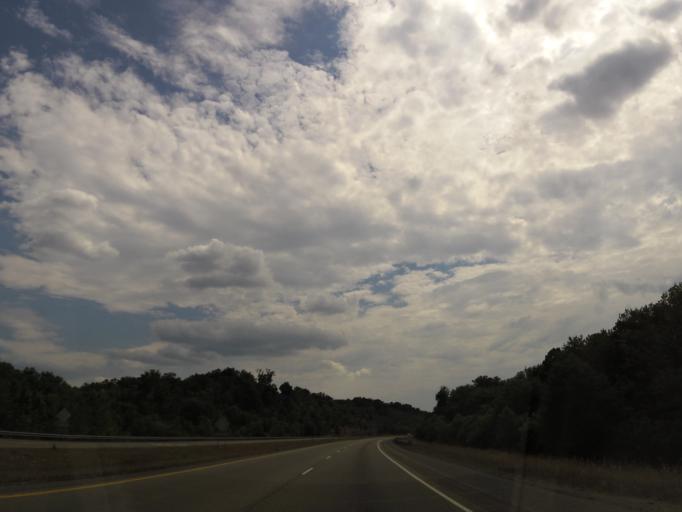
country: US
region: Tennessee
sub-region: Marion County
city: South Pittsburg
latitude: 34.9967
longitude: -85.7055
